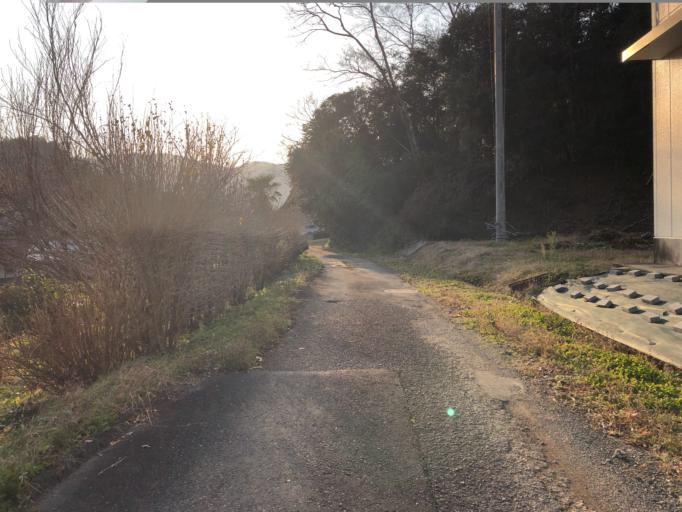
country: JP
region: Kyoto
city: Kameoka
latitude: 35.0595
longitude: 135.4830
